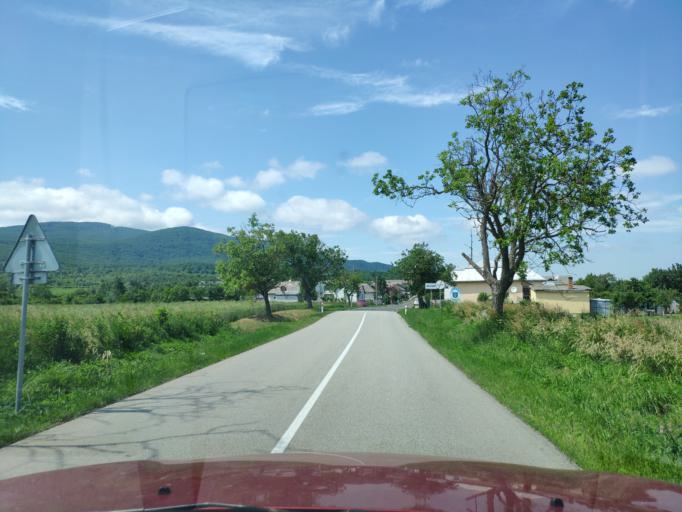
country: SK
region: Kosicky
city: Secovce
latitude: 48.7550
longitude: 21.6434
